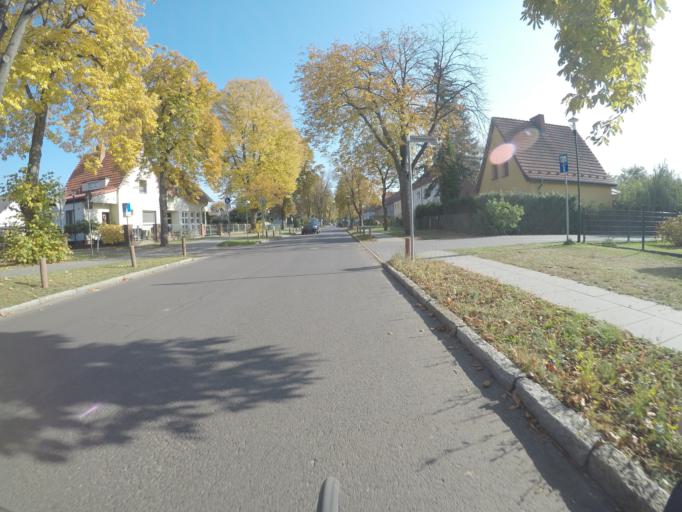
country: DE
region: Brandenburg
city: Hohen Neuendorf
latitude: 52.6801
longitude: 13.2494
